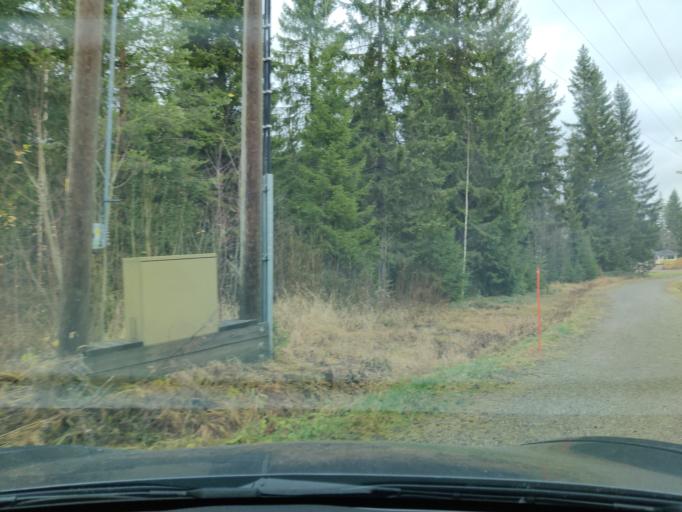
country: FI
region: Northern Savo
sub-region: Ylae-Savo
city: Kiuruvesi
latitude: 63.6407
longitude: 26.6387
